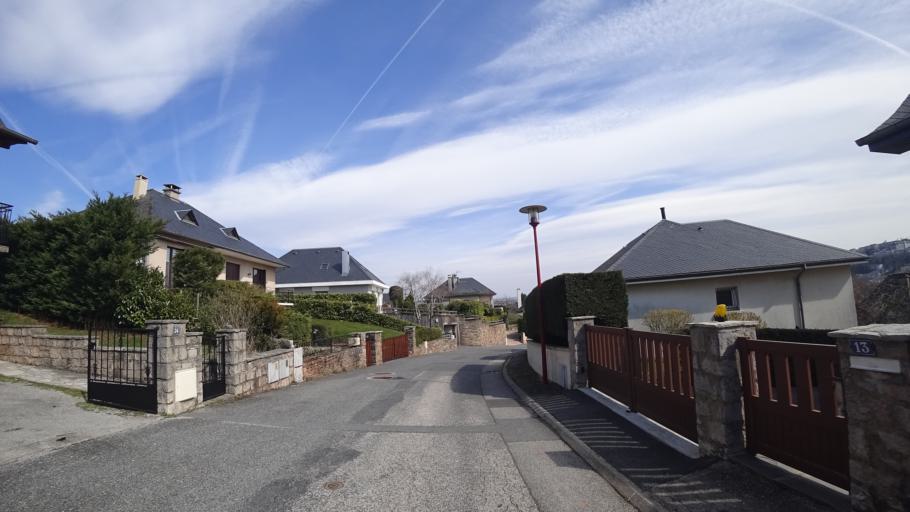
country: FR
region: Midi-Pyrenees
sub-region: Departement de l'Aveyron
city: Rodez
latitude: 44.3666
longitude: 2.5637
